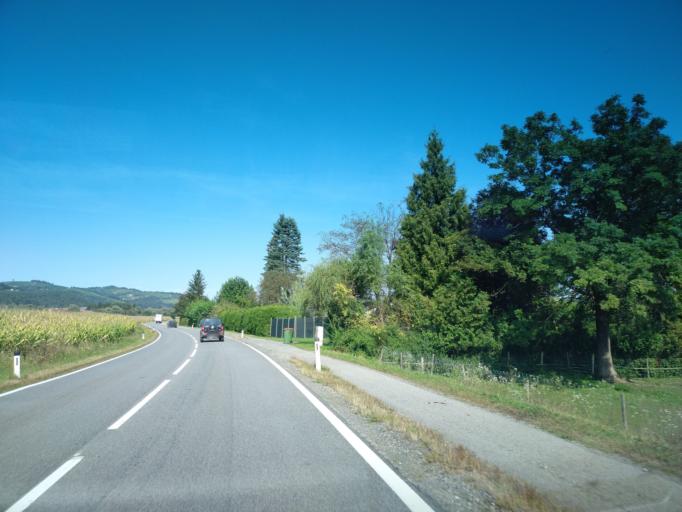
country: AT
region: Styria
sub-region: Politischer Bezirk Leibnitz
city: Heimschuh
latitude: 46.7526
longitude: 15.4772
